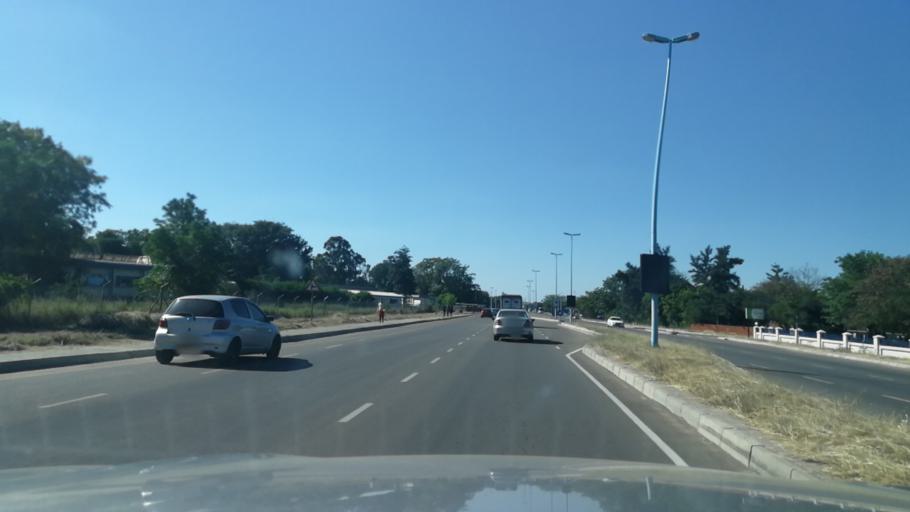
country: BW
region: South East
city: Gaborone
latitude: -24.6753
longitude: 25.9217
